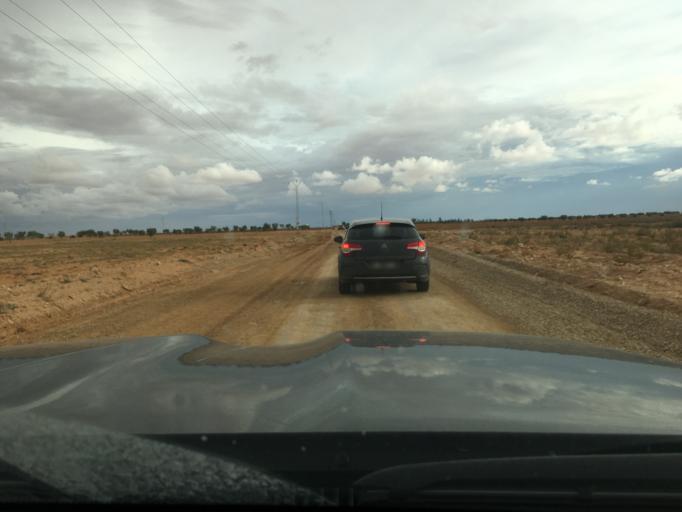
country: TN
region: Madanin
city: Medenine
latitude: 33.2795
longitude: 10.5564
